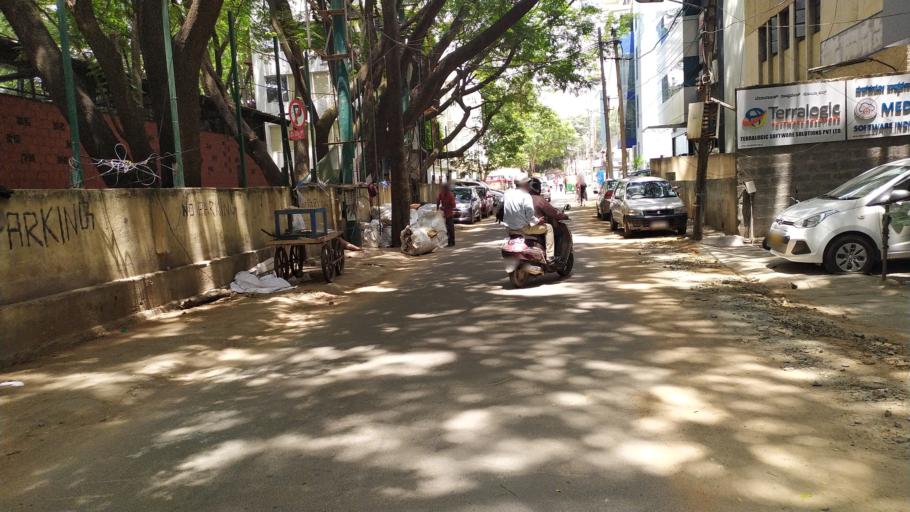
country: IN
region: Karnataka
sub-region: Bangalore Urban
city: Bangalore
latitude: 12.9350
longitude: 77.6151
